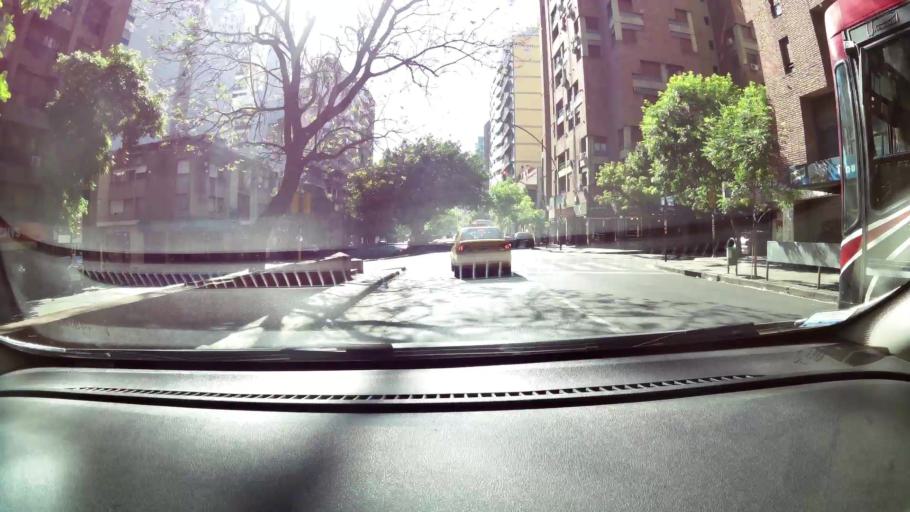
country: AR
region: Cordoba
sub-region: Departamento de Capital
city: Cordoba
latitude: -31.4208
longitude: -64.1864
